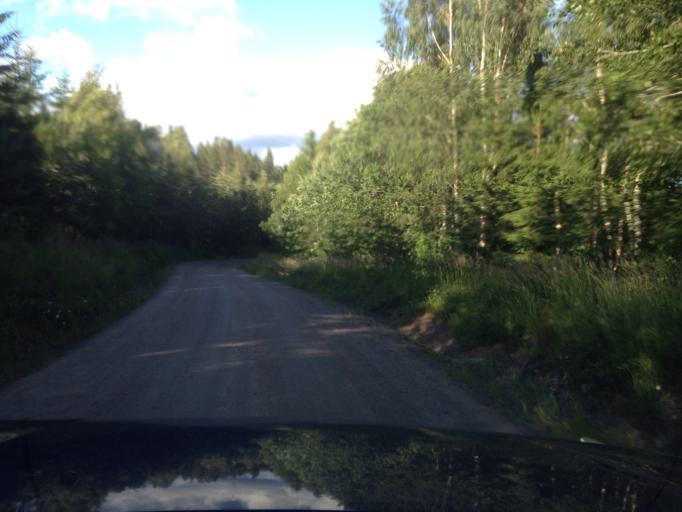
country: SE
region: Dalarna
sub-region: Ludvika Kommun
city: Abborrberget
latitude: 60.2334
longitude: 14.8172
